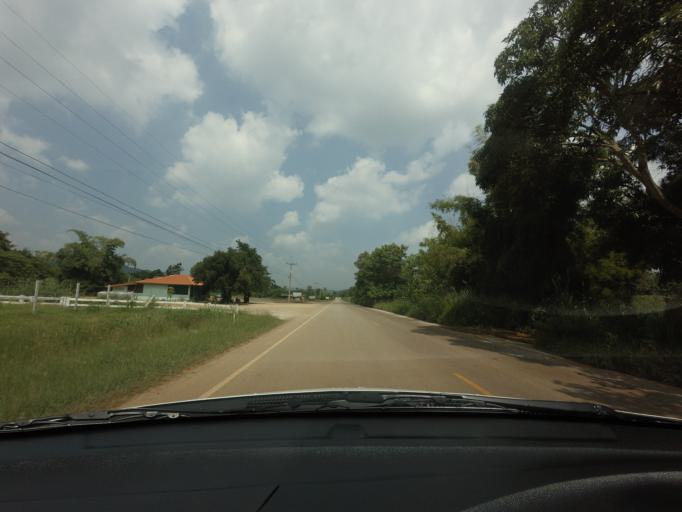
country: TH
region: Nakhon Ratchasima
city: Pak Chong
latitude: 14.5578
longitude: 101.5728
